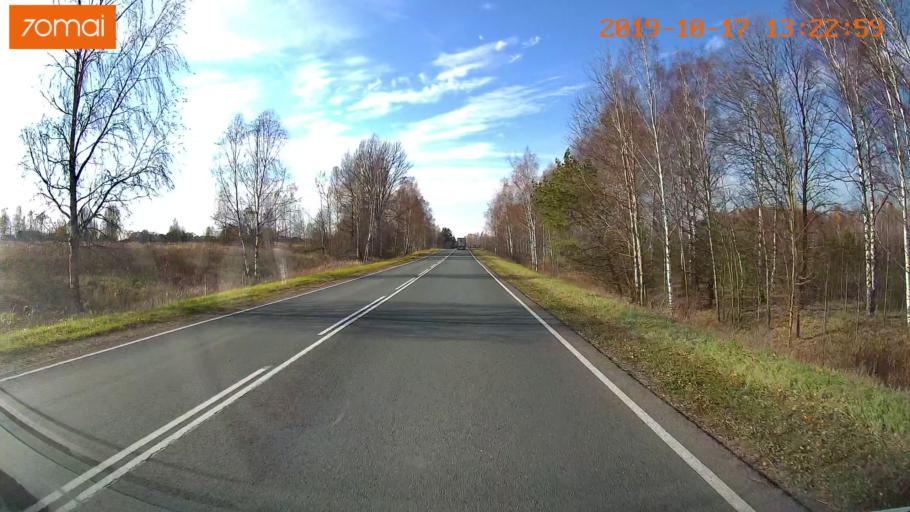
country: RU
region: Rjazan
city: Gus'-Zheleznyy
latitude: 55.0876
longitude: 40.9889
